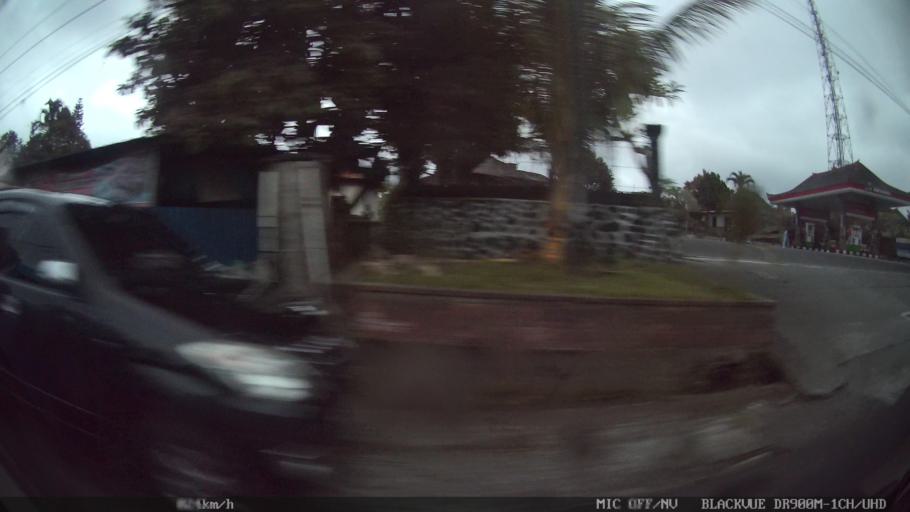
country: ID
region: Bali
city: Banjar Buahan
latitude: -8.4087
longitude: 115.2453
